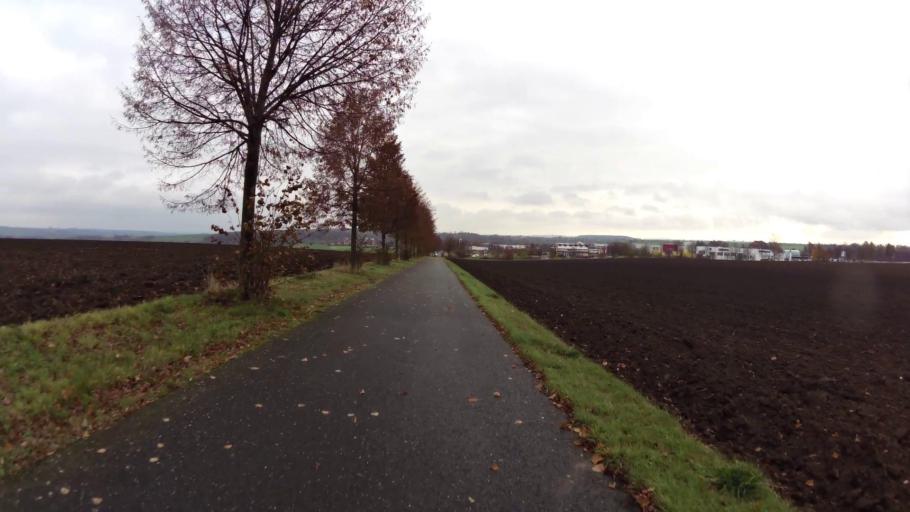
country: DE
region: Thuringia
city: Kromsdorf
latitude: 50.9828
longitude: 11.3749
